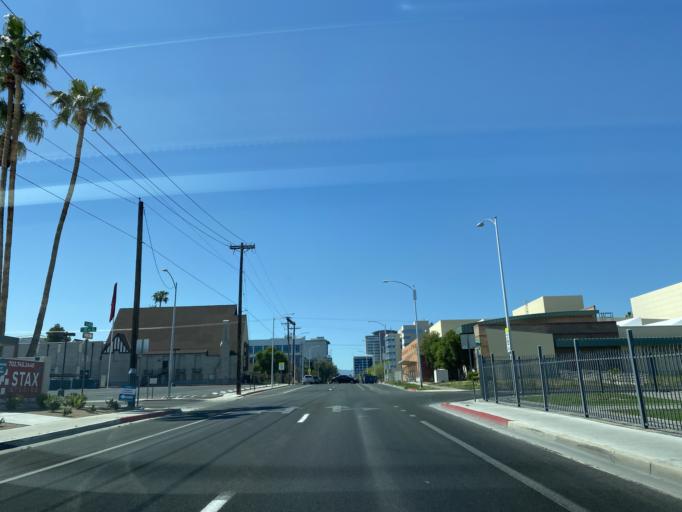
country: US
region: Nevada
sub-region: Clark County
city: Las Vegas
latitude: 36.1620
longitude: -115.1376
